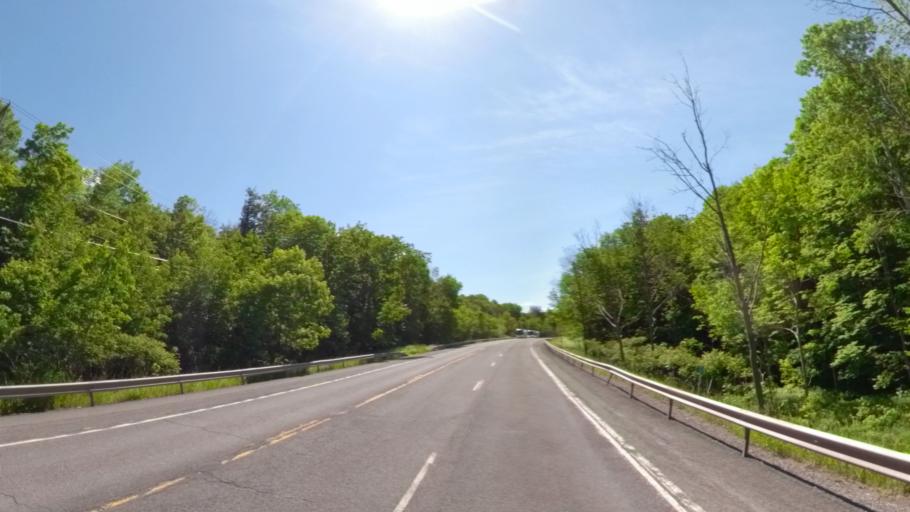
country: US
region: New York
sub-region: Delaware County
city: Stamford
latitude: 42.1492
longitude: -74.4976
